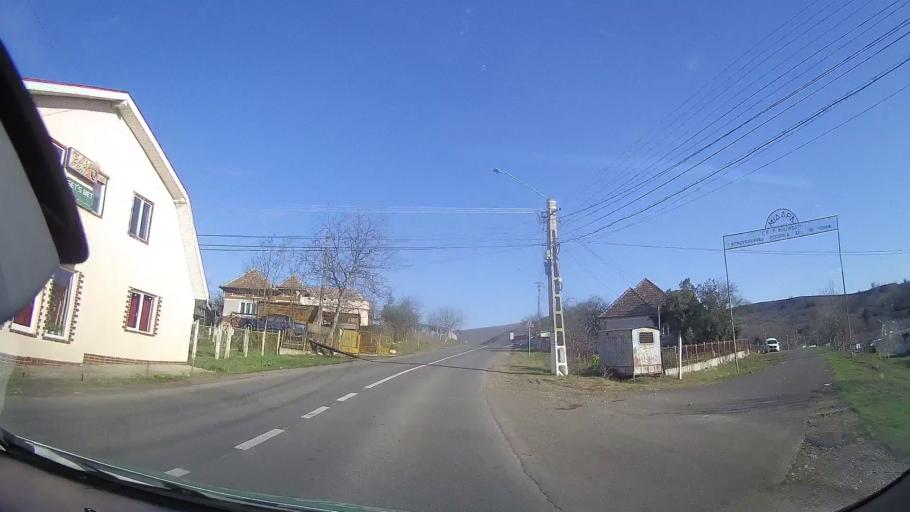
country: RO
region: Mures
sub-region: Comuna Zau De Campie
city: Zau de Campie
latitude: 46.6193
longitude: 24.1291
